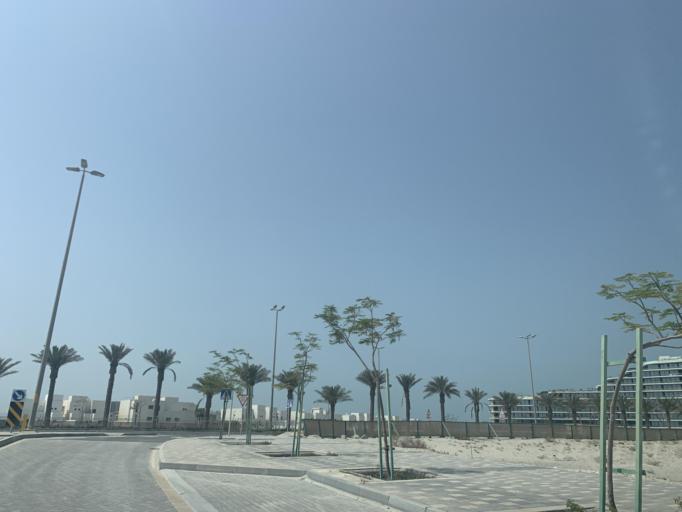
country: BH
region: Muharraq
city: Al Hadd
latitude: 26.2721
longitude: 50.6711
